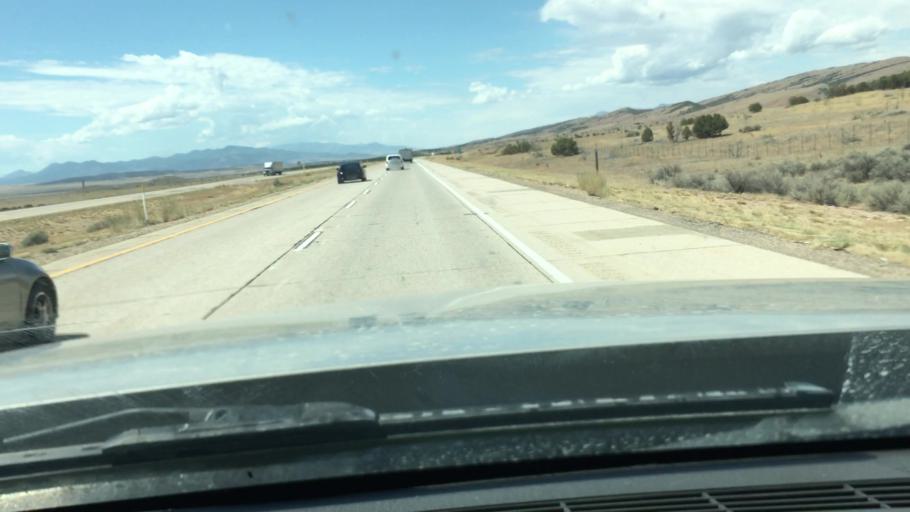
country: US
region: Utah
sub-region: Juab County
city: Nephi
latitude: 39.5709
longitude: -111.9369
